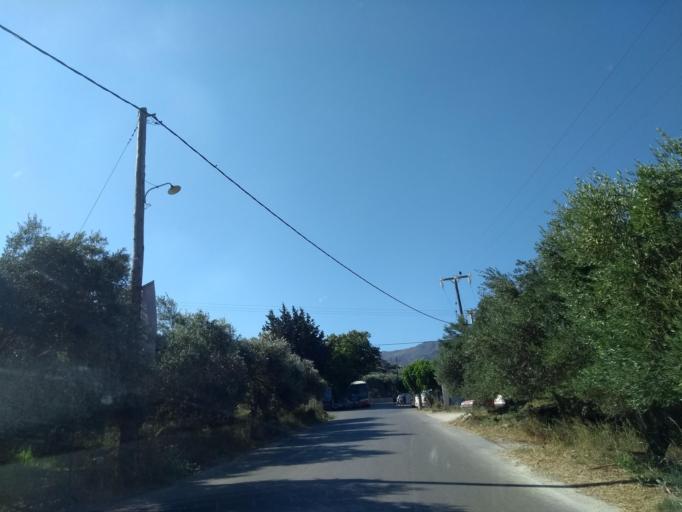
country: GR
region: Crete
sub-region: Nomos Chanias
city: Georgioupolis
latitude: 35.3336
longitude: 24.2811
